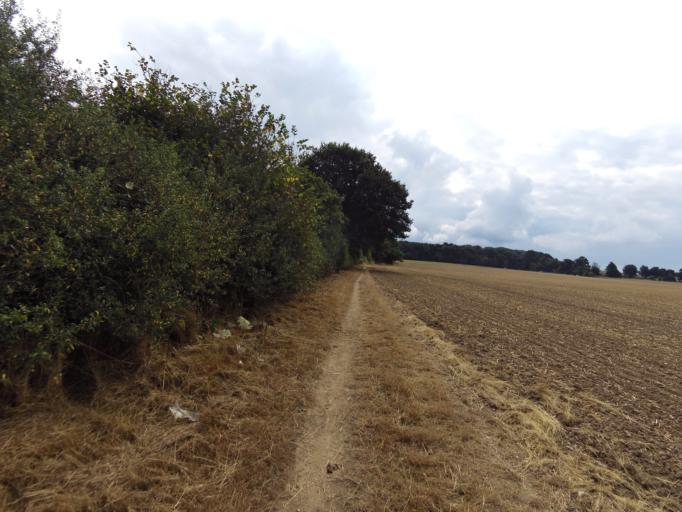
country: GB
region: England
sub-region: Hertfordshire
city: Shenley AV
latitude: 51.7128
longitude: -0.2666
